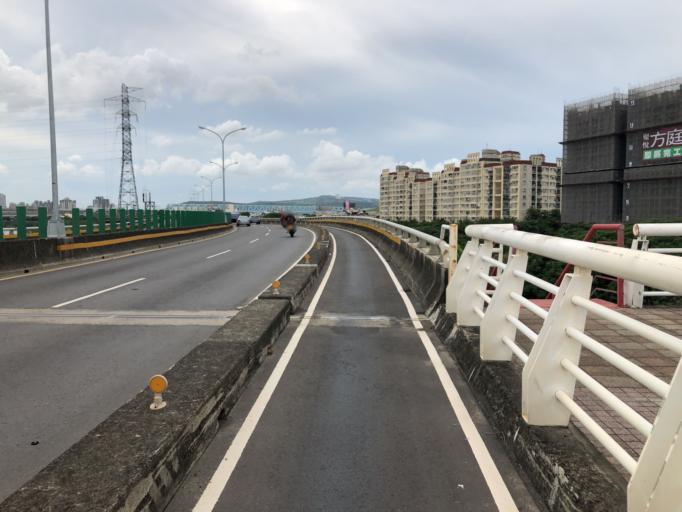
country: TW
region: Taiwan
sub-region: Changhua
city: Chang-hua
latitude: 24.0995
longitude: 120.6252
